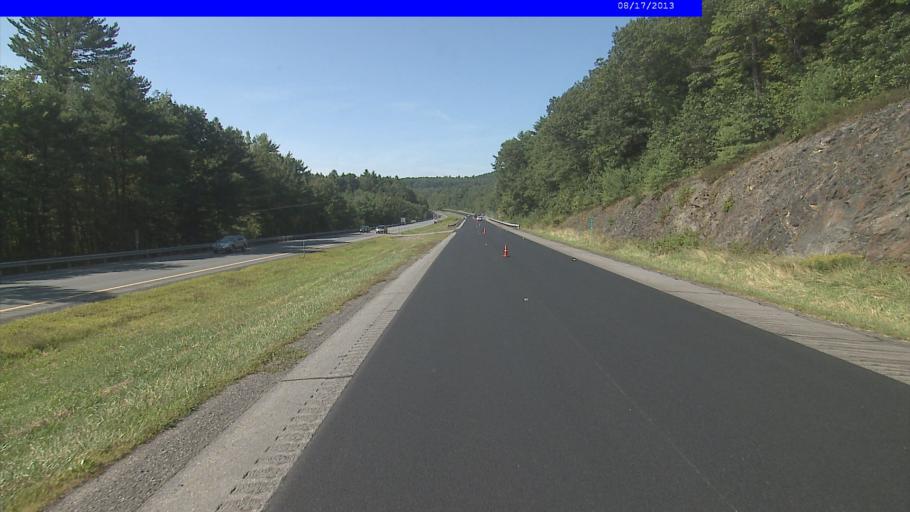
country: US
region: Vermont
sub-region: Windham County
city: Bellows Falls
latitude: 43.1600
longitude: -72.4666
